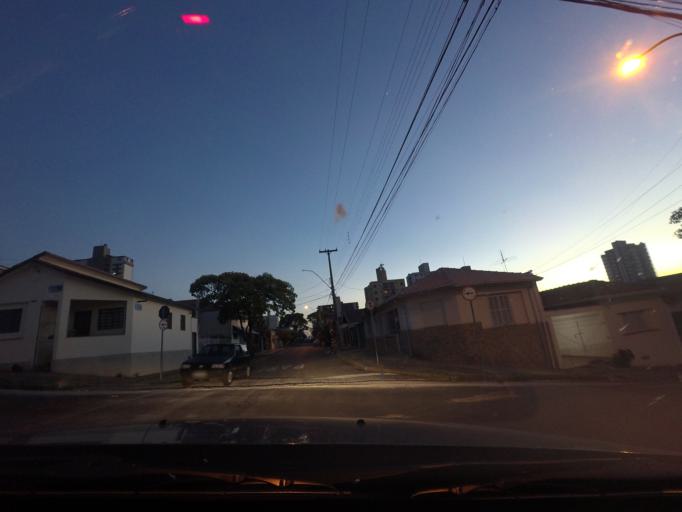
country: BR
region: Sao Paulo
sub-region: Piracicaba
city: Piracicaba
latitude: -22.7181
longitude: -47.6350
